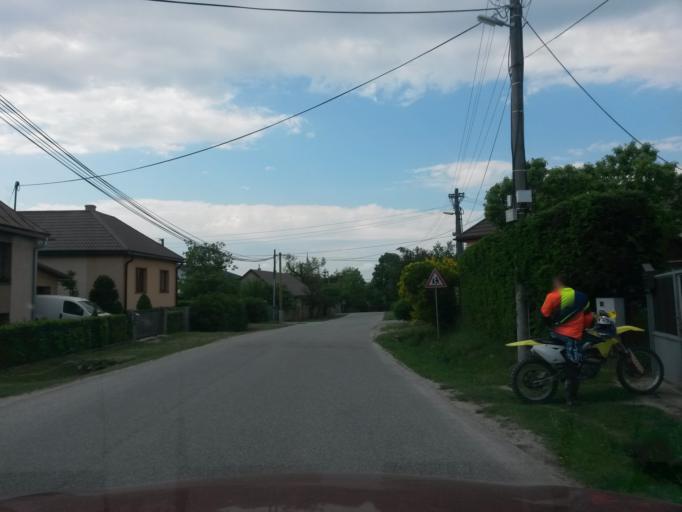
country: SK
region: Kosicky
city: Moldava nad Bodvou
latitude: 48.6937
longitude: 21.0106
